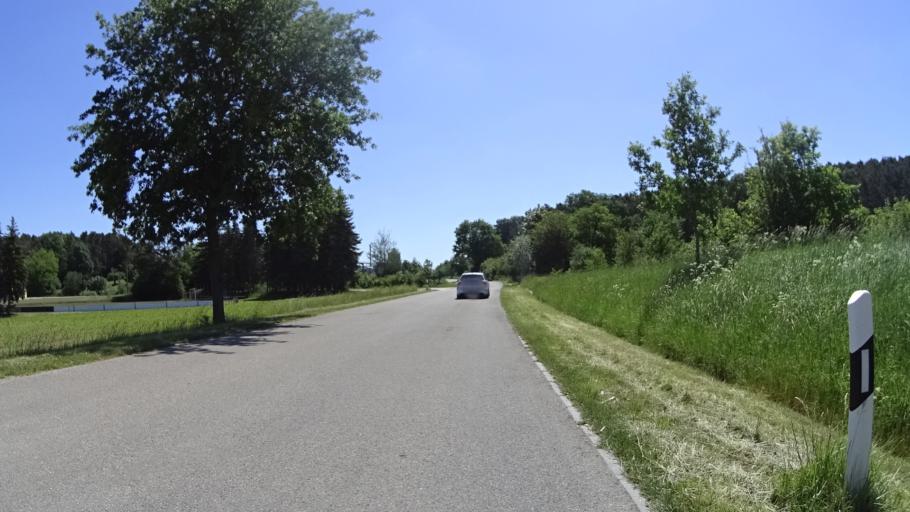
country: DE
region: Bavaria
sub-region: Regierungsbezirk Mittelfranken
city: Pfofeld
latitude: 49.1178
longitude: 10.8640
